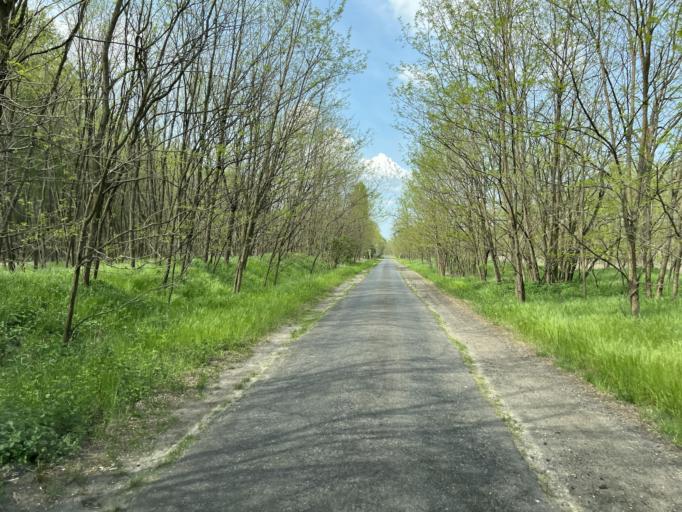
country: HU
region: Pest
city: Kocser
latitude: 47.0503
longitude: 19.9002
